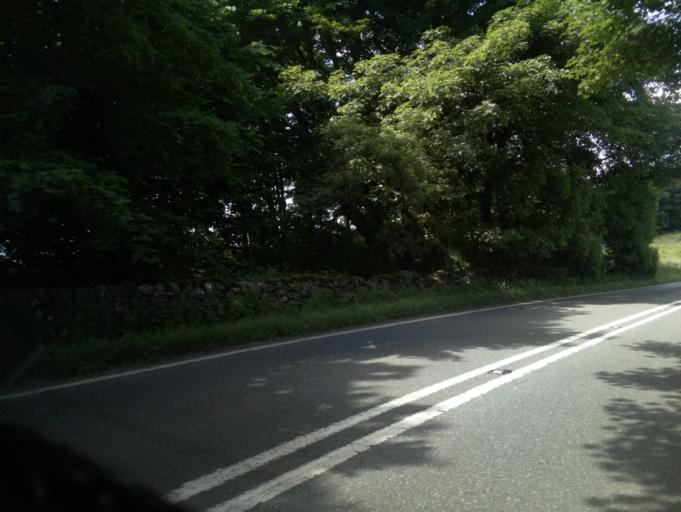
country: GB
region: England
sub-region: Derbyshire
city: Ashbourne
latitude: 53.0945
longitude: -1.7728
